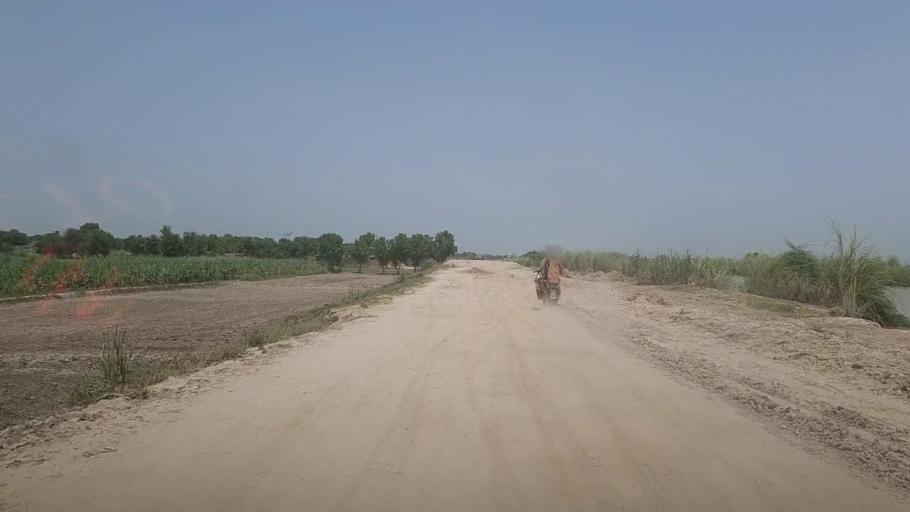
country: PK
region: Sindh
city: Pad Idan
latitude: 26.8046
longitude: 68.2720
